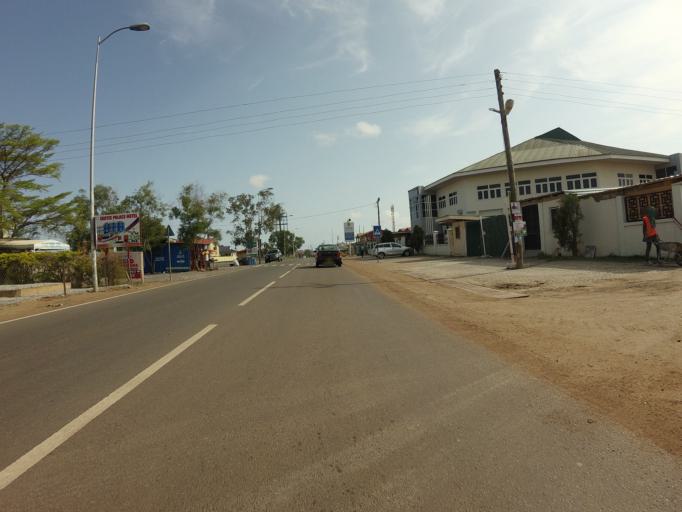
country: GH
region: Greater Accra
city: Nungua
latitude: 5.6501
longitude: -0.0763
